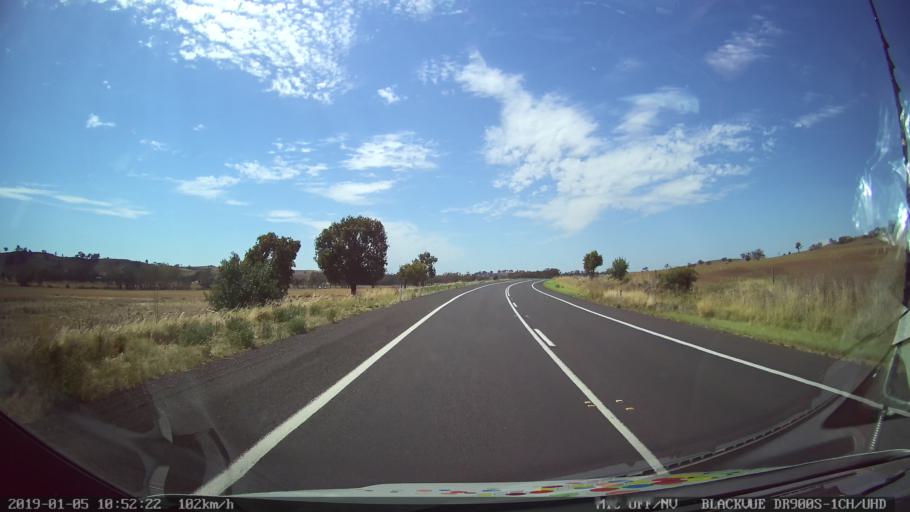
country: AU
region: New South Wales
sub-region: Warrumbungle Shire
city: Coonabarabran
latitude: -31.4307
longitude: 149.1029
